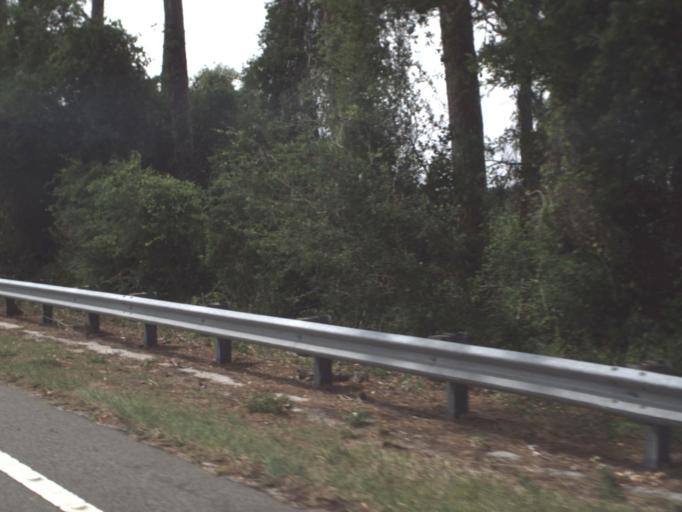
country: US
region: Florida
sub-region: Putnam County
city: Crescent City
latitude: 29.4811
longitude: -81.4152
